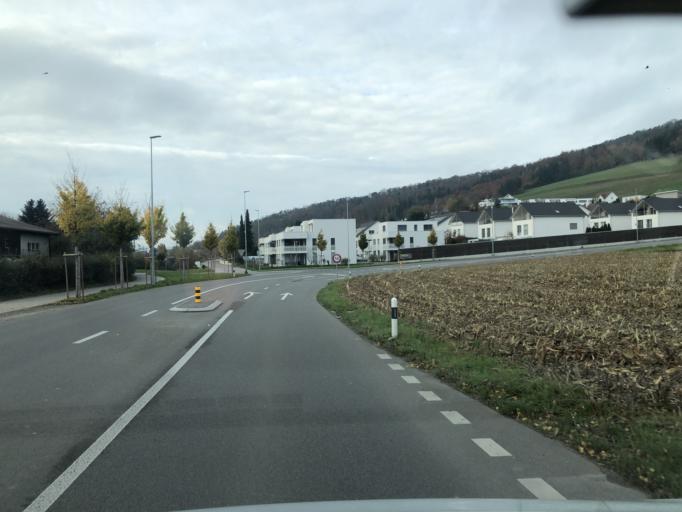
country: CH
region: Aargau
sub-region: Bezirk Baden
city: Birmenstorf
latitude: 47.4557
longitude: 8.2631
